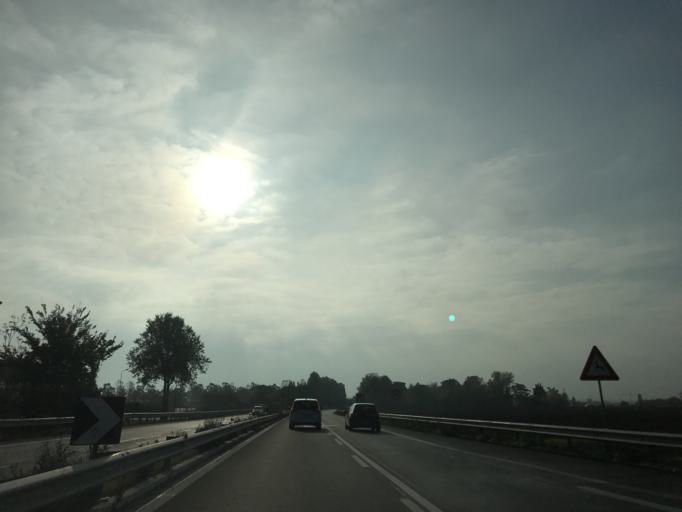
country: IT
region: Emilia-Romagna
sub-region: Provincia di Rimini
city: Bellaria-Igea Marina
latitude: 44.1117
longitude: 12.4811
